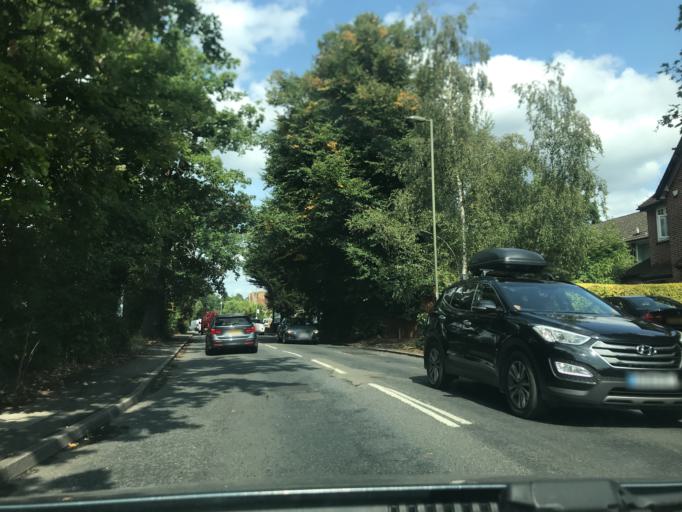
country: GB
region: England
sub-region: Surrey
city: Byfleet
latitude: 51.3529
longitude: -0.4587
